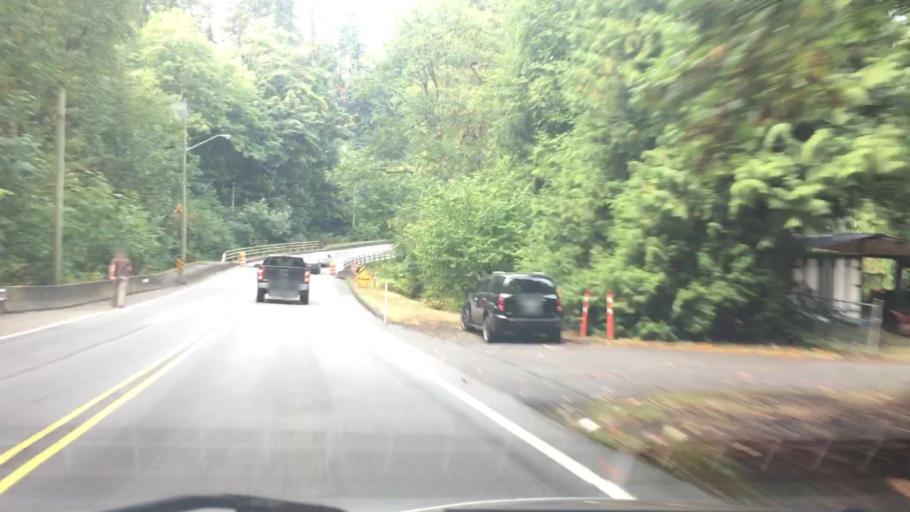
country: CA
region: British Columbia
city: Langley
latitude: 49.1027
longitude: -122.5474
